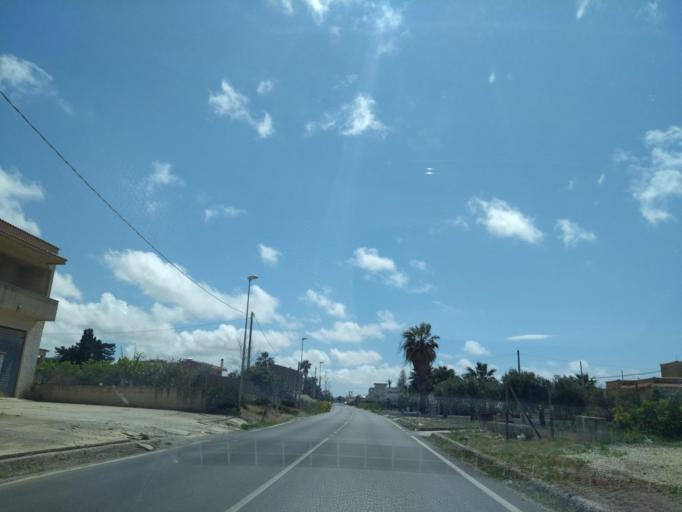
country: IT
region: Sicily
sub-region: Trapani
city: Marsala
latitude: 37.8681
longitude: 12.5177
